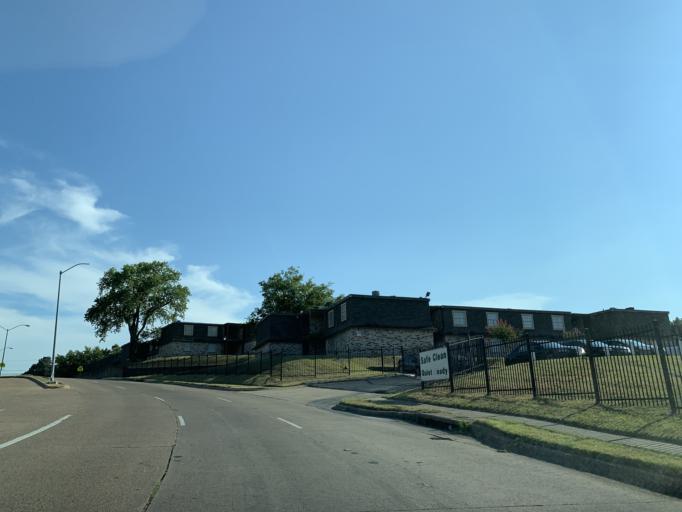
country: US
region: Texas
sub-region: Dallas County
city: Hutchins
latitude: 32.6810
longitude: -96.8058
